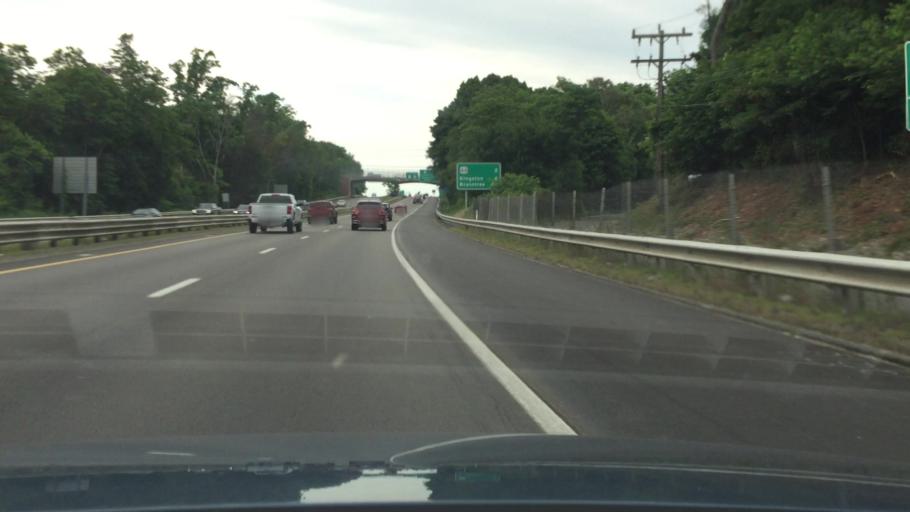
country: US
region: Massachusetts
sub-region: Plymouth County
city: Plymouth
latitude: 41.9472
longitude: -70.6775
